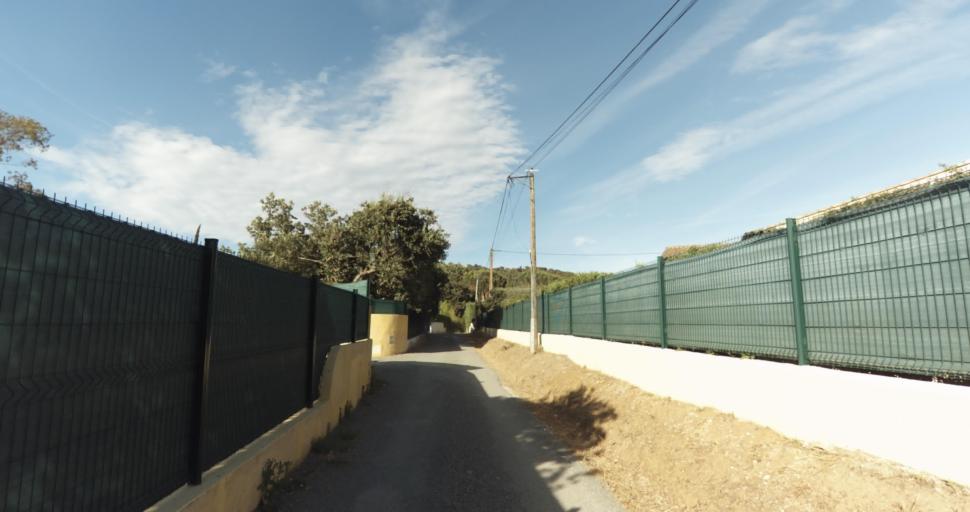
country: FR
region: Provence-Alpes-Cote d'Azur
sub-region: Departement du Var
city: Gassin
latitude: 43.2226
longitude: 6.5732
